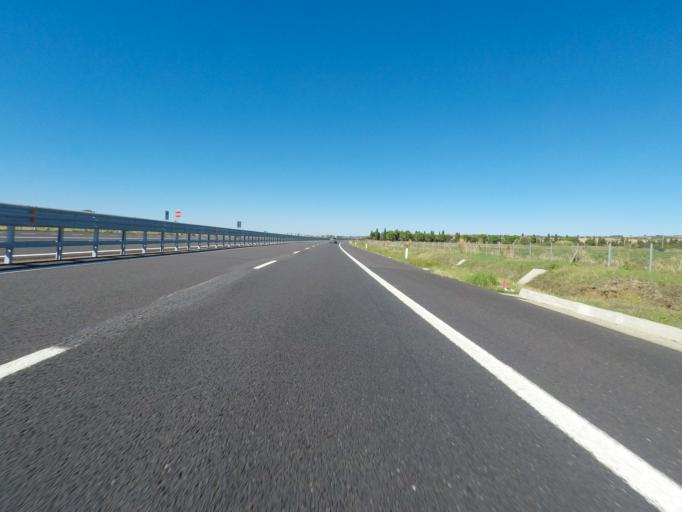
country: IT
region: Latium
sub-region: Provincia di Viterbo
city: Tarquinia
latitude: 42.2170
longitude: 11.7739
